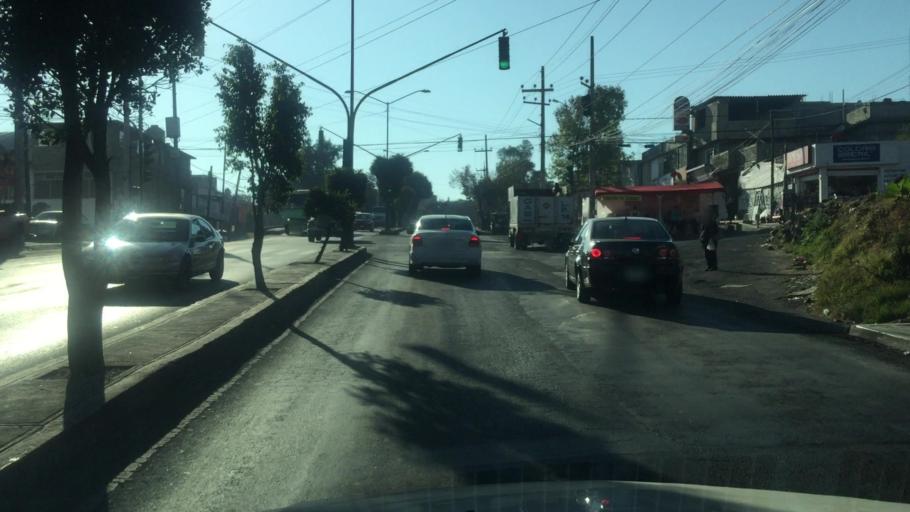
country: MX
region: Mexico City
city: Tlalpan
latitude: 19.2743
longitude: -99.2072
